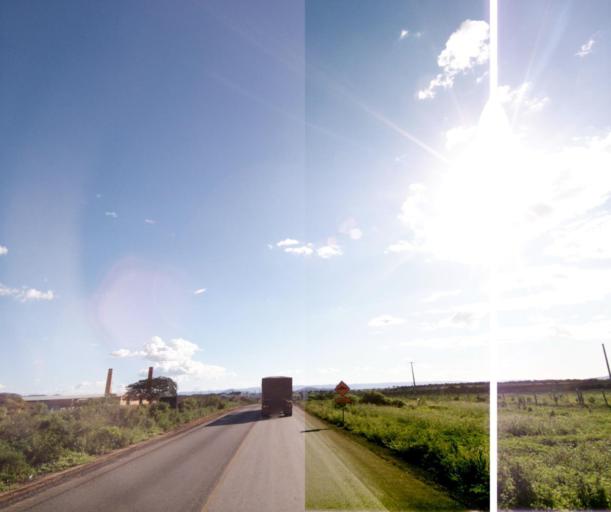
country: BR
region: Bahia
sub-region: Guanambi
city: Guanambi
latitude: -14.1809
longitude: -42.7345
